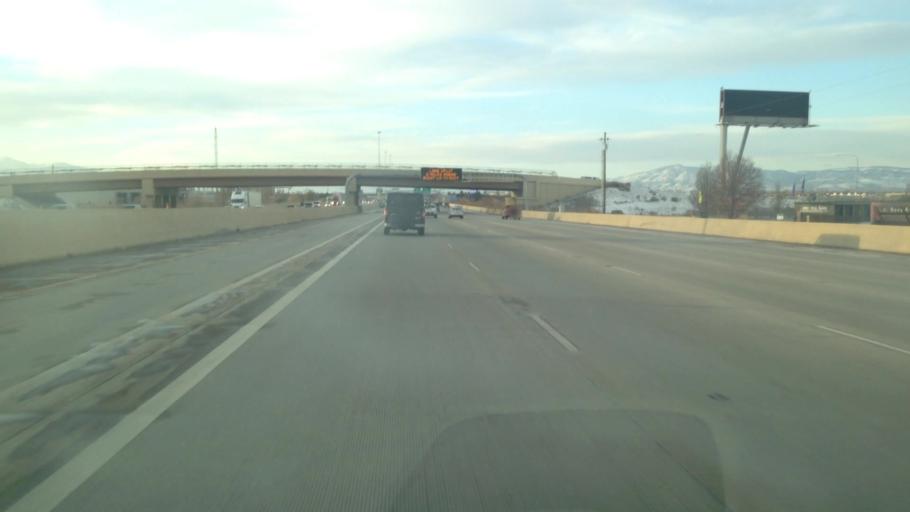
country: US
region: Utah
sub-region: Utah County
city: Pleasant Grove
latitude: 40.3434
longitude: -111.7585
